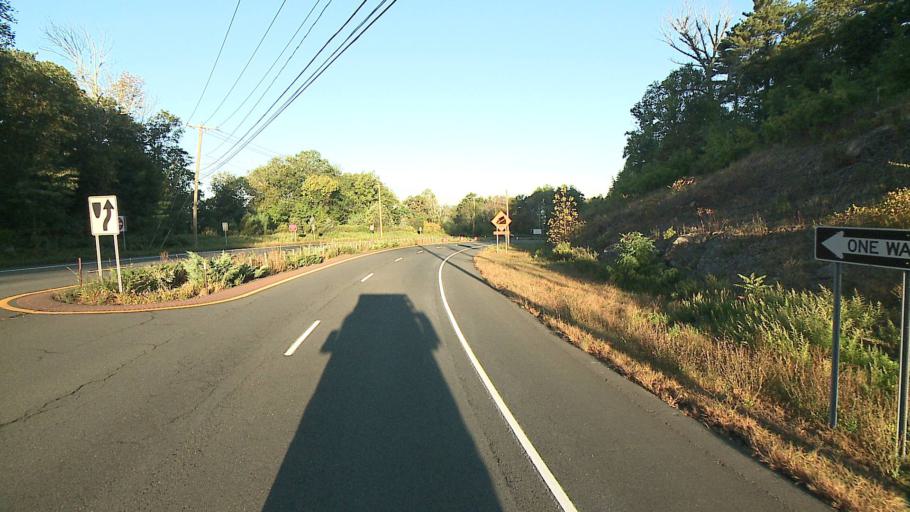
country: US
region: Connecticut
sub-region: Hartford County
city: Weatogue
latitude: 41.7978
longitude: -72.8015
